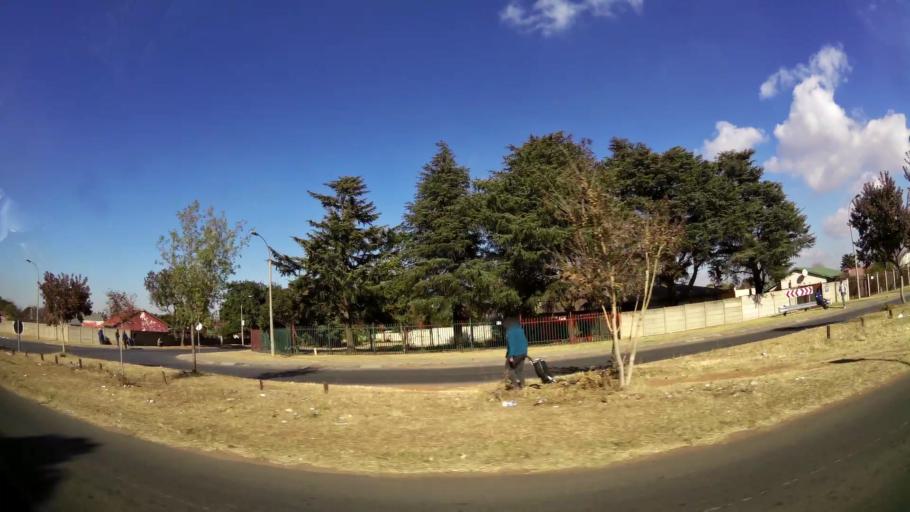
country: ZA
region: Gauteng
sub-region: City of Johannesburg Metropolitan Municipality
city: Roodepoort
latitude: -26.1495
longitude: 27.8272
